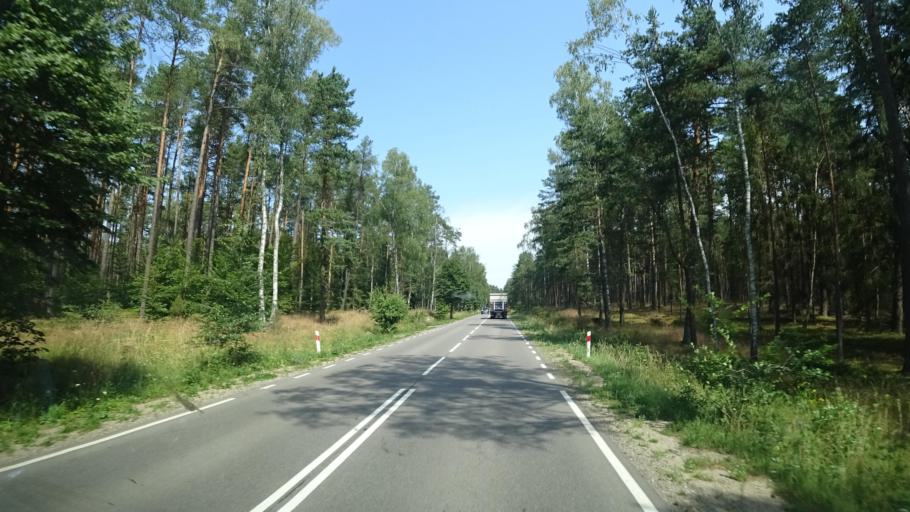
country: PL
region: Pomeranian Voivodeship
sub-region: Powiat koscierski
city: Lipusz
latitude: 54.1104
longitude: 17.8287
